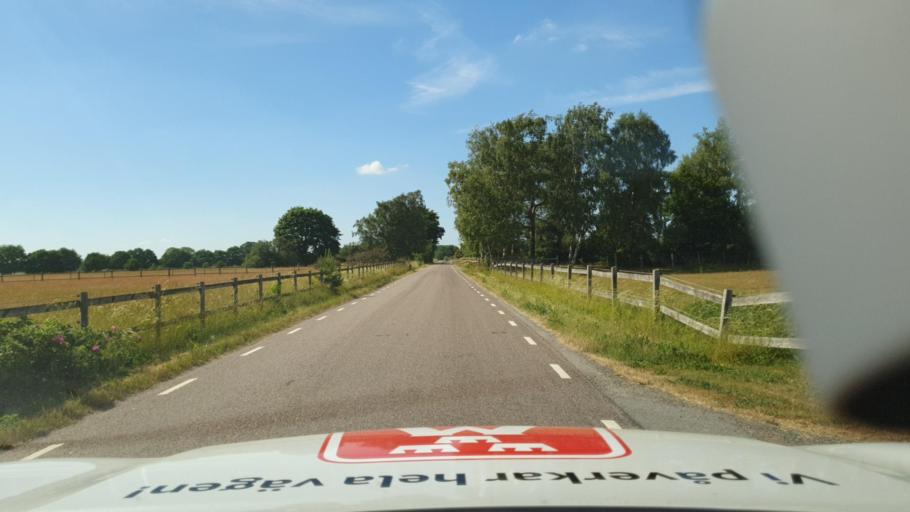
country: SE
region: Skane
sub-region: Sjobo Kommun
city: Blentarp
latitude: 55.6213
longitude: 13.6303
